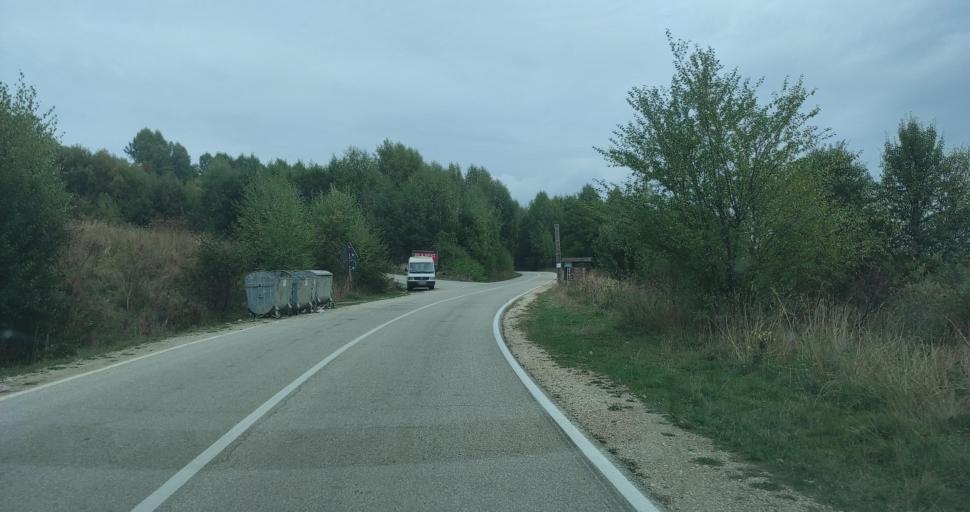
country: RS
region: Central Serbia
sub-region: Jablanicki Okrug
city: Crna Trava
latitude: 42.7117
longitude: 22.3277
